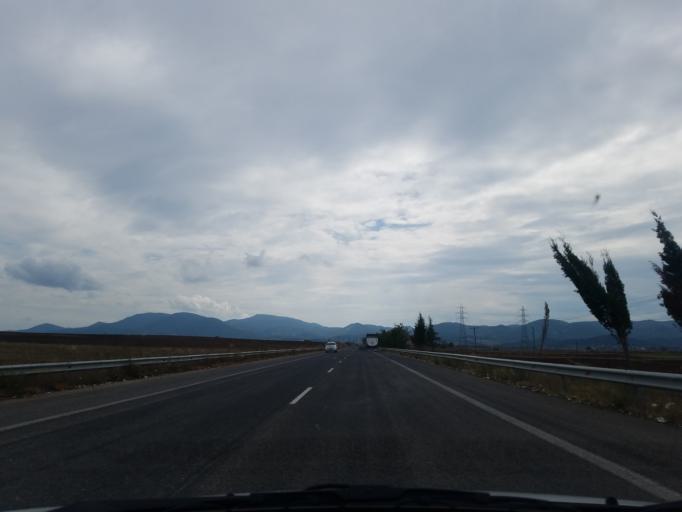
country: GR
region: Central Greece
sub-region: Nomos Fthiotidos
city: Omvriaki
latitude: 39.0643
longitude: 22.3278
